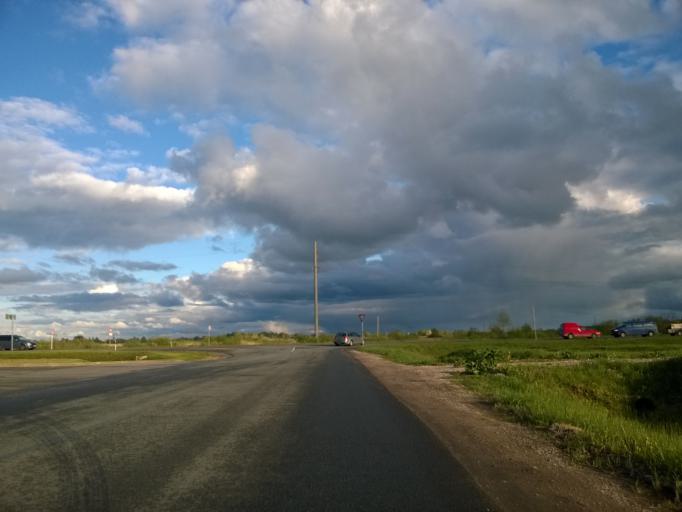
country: LV
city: Tireli
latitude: 56.9303
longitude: 23.5867
